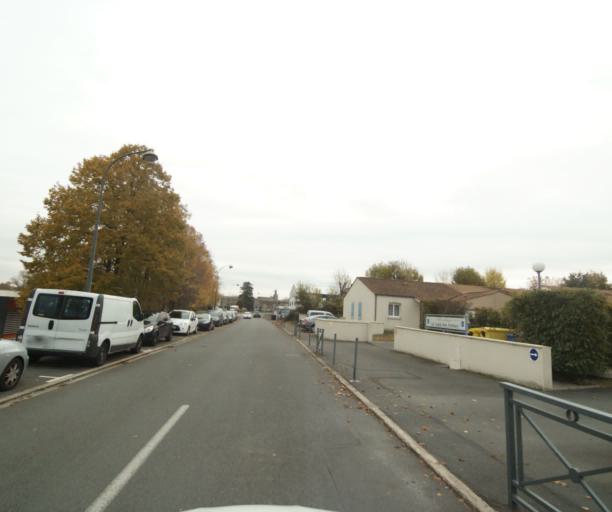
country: FR
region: Poitou-Charentes
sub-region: Departement de la Charente-Maritime
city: Saintes
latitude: 45.7455
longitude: -0.6526
